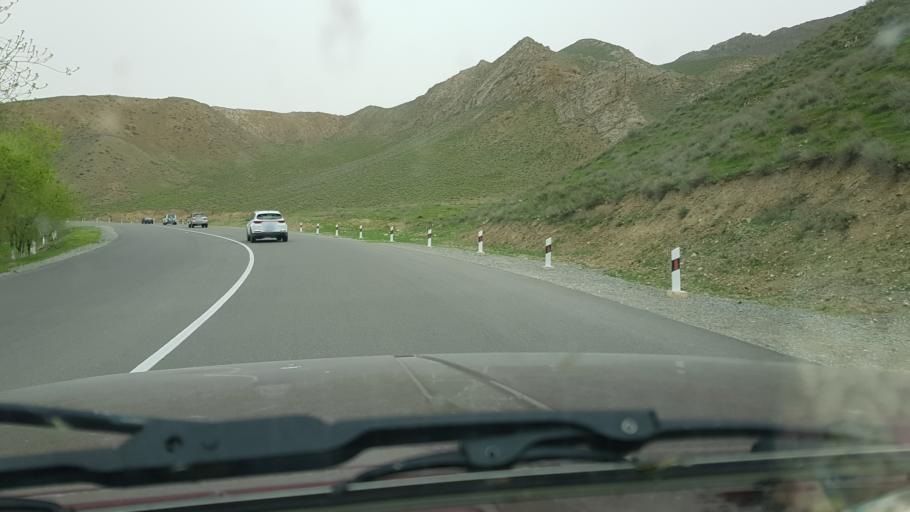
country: TM
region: Ahal
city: Arcabil
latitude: 38.0180
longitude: 58.0067
